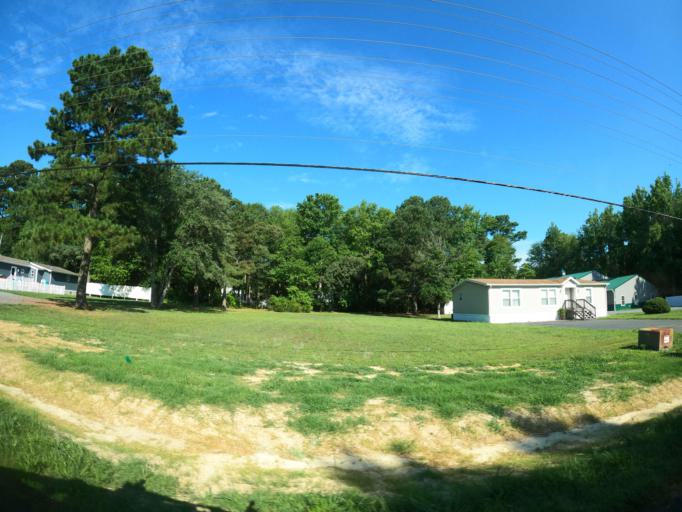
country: US
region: Delaware
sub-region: Sussex County
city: Ocean View
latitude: 38.5229
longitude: -75.0960
